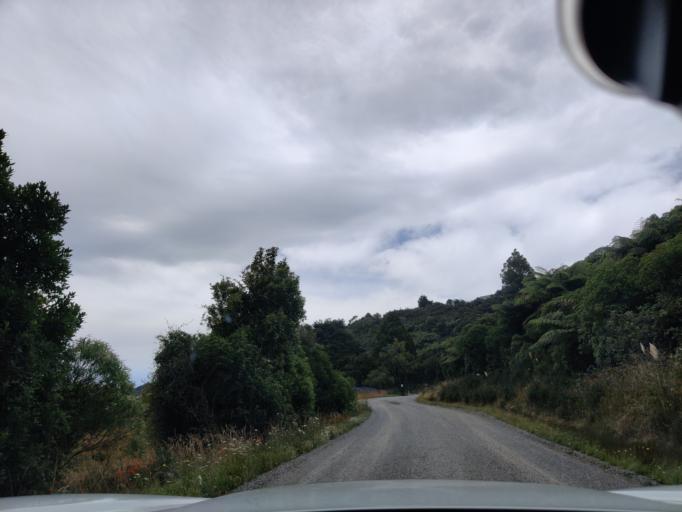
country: NZ
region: Wellington
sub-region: Masterton District
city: Masterton
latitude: -41.0392
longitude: 175.4134
